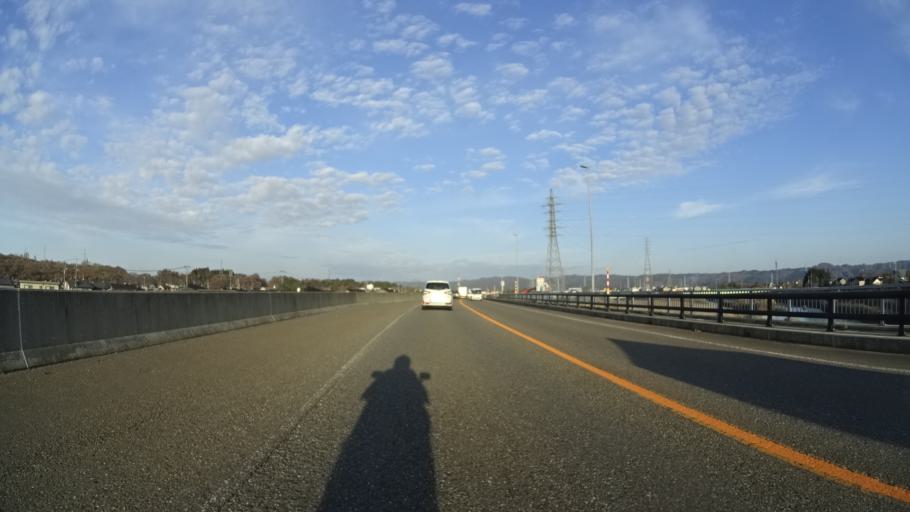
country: JP
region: Niigata
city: Kashiwazaki
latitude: 37.3894
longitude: 138.5924
